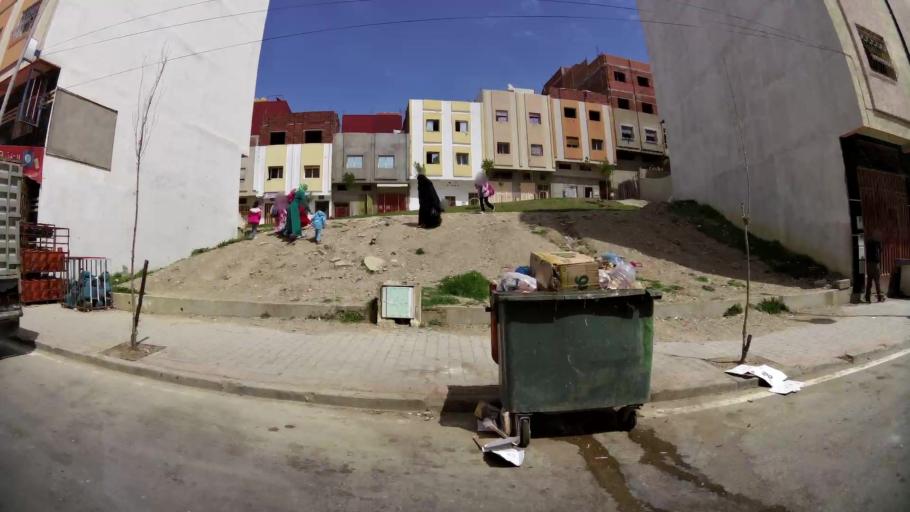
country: MA
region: Tanger-Tetouan
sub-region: Tanger-Assilah
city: Tangier
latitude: 35.7352
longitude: -5.8182
